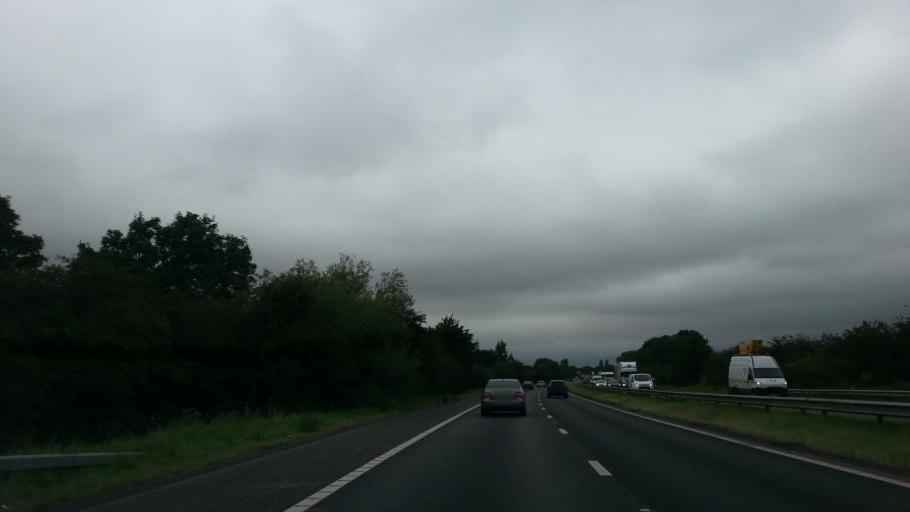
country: GB
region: England
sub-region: Doncaster
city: Tickhill
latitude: 53.4247
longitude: -1.0929
